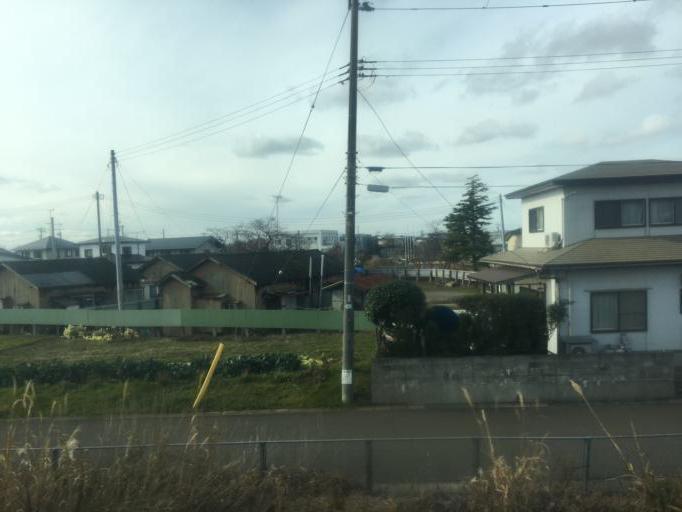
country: JP
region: Akita
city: Tenno
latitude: 39.9422
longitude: 140.0799
